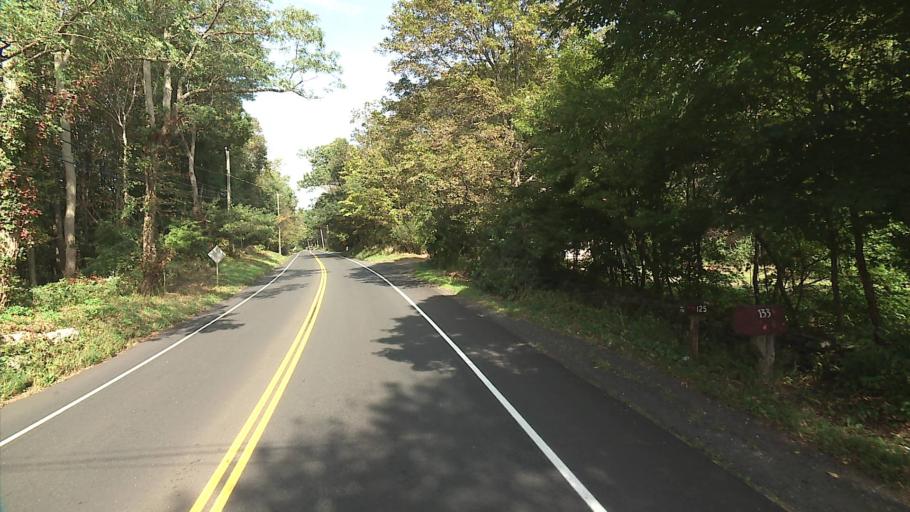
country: US
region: Connecticut
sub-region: Fairfield County
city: Newtown
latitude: 41.3980
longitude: -73.2423
